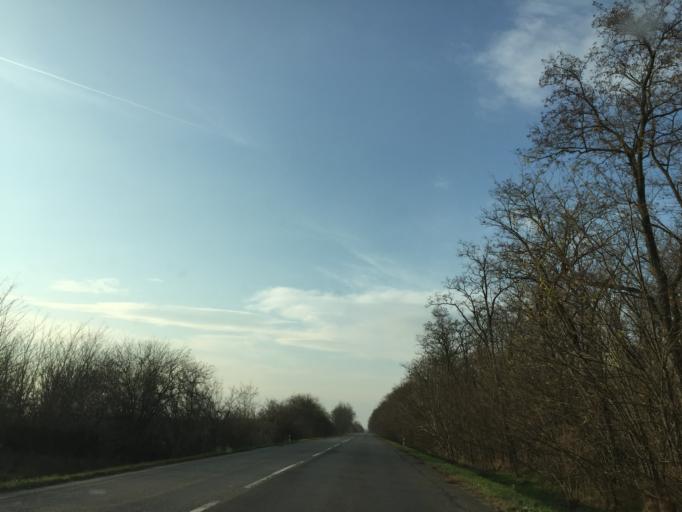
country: SK
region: Nitriansky
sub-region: Okres Komarno
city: Hurbanovo
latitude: 47.9254
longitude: 18.2267
